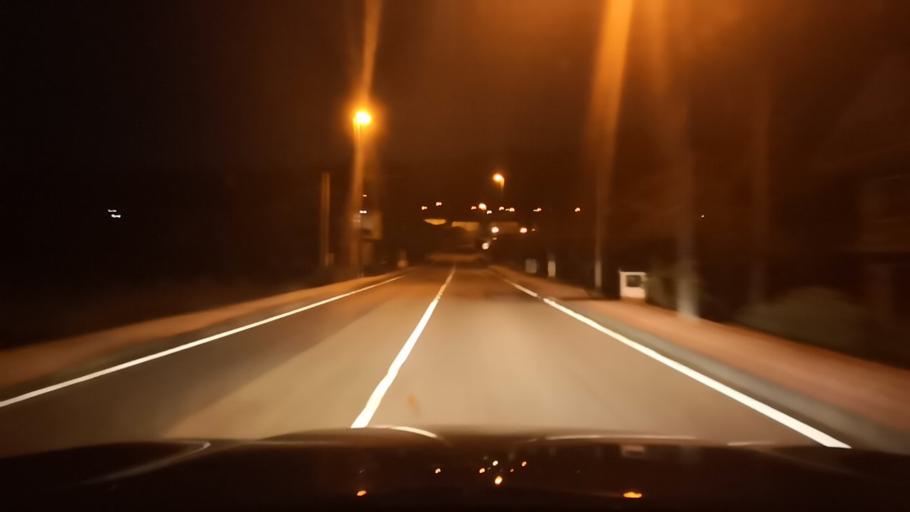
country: ES
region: Galicia
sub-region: Provincia de Ourense
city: Verin
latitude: 41.9374
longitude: -7.4126
